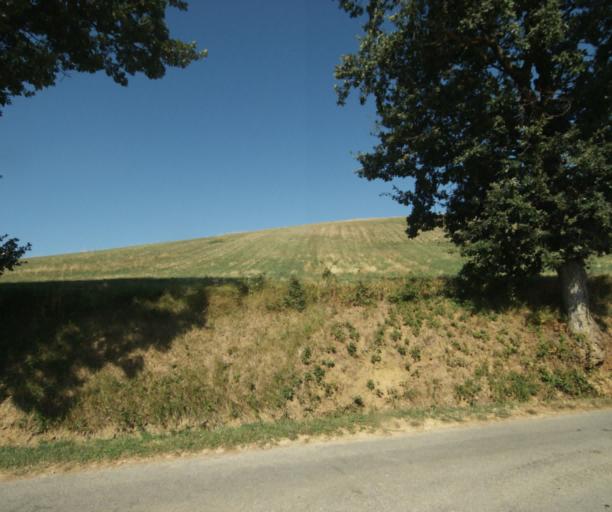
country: FR
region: Midi-Pyrenees
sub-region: Departement de la Haute-Garonne
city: Saint-Felix-Lauragais
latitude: 43.5174
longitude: 1.9349
